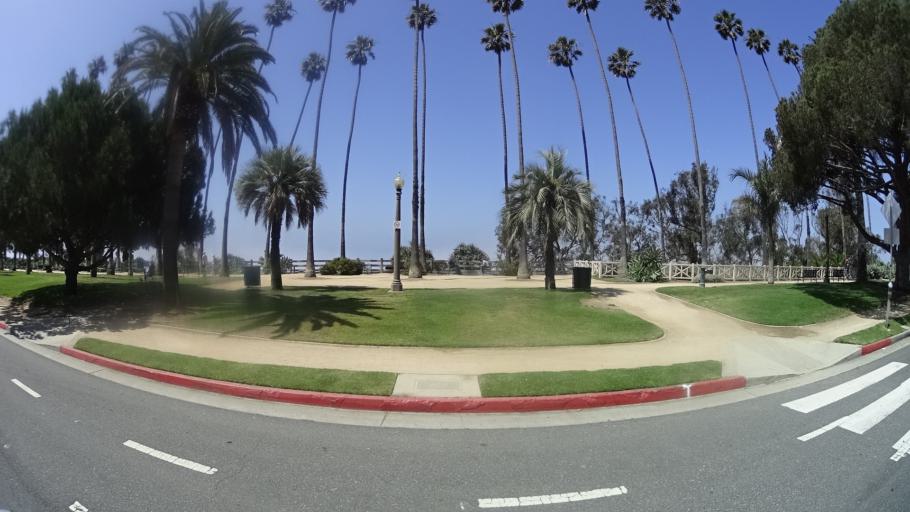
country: US
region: California
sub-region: Los Angeles County
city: Santa Monica
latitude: 34.0247
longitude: -118.5113
